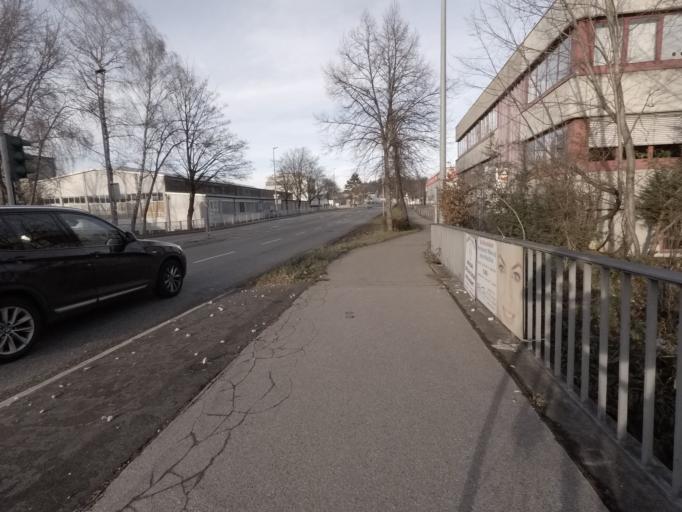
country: DE
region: Baden-Wuerttemberg
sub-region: Tuebingen Region
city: Pfullingen
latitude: 48.4786
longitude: 9.2289
